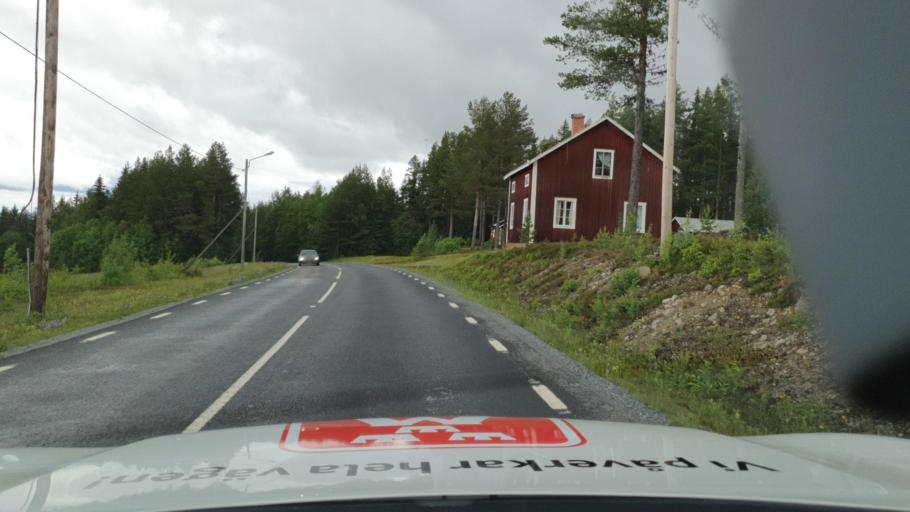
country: SE
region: Vaesterbotten
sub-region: Dorotea Kommun
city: Dorotea
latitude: 64.2373
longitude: 16.5412
